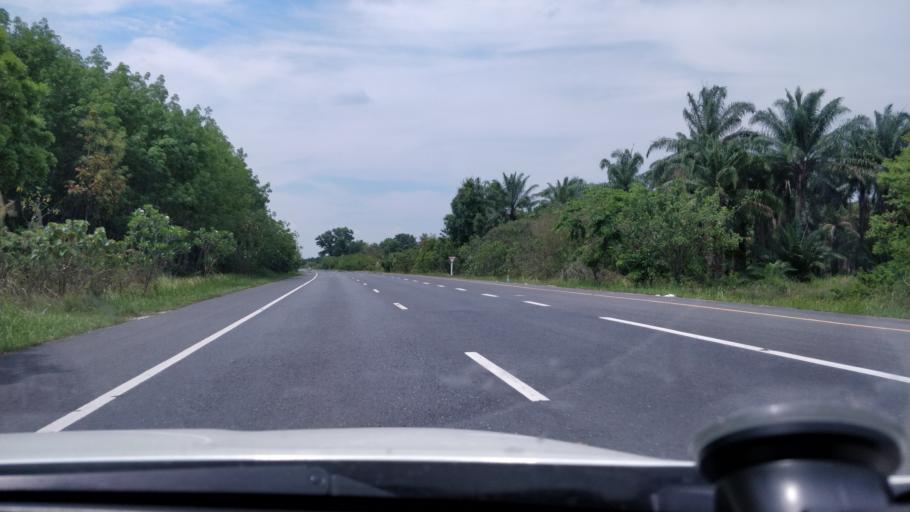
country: TH
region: Surat Thani
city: Khian Sa
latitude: 8.7326
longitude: 99.1602
